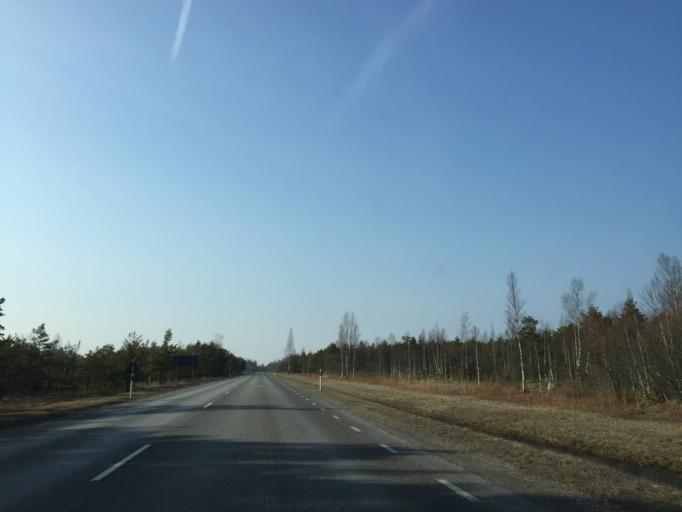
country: EE
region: Saare
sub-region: Orissaare vald
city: Orissaare
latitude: 58.5776
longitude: 23.3670
